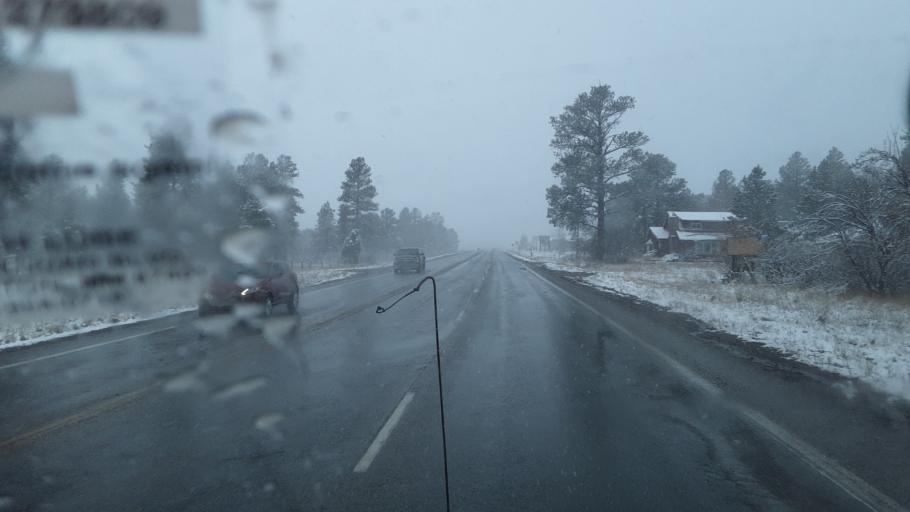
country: US
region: Colorado
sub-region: Archuleta County
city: Pagosa Springs
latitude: 37.2729
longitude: -107.0371
